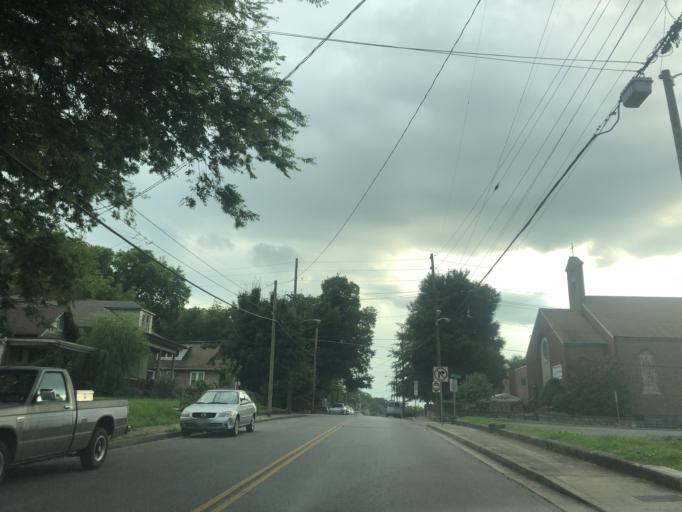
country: US
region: Tennessee
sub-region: Davidson County
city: Nashville
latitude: 36.1722
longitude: -86.8044
